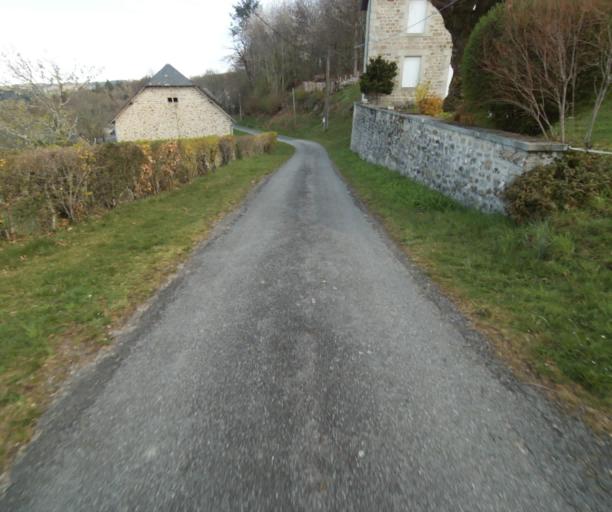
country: FR
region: Limousin
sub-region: Departement de la Correze
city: Correze
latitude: 45.3637
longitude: 1.8517
